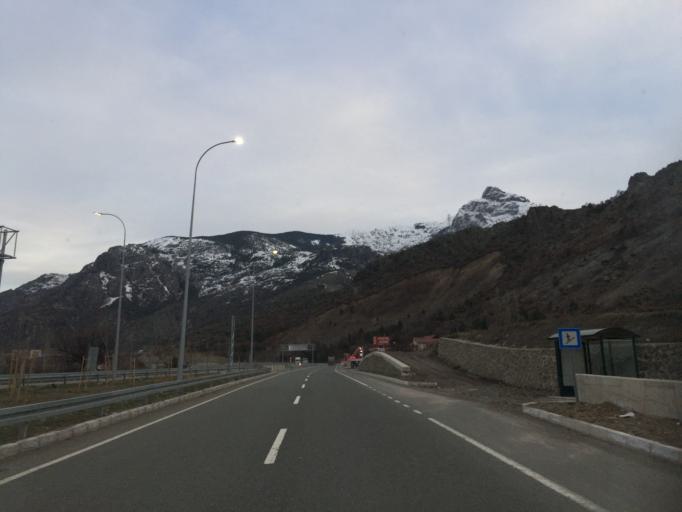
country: TR
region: Gumushane
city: Gumushkhane
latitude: 40.5082
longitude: 39.4219
